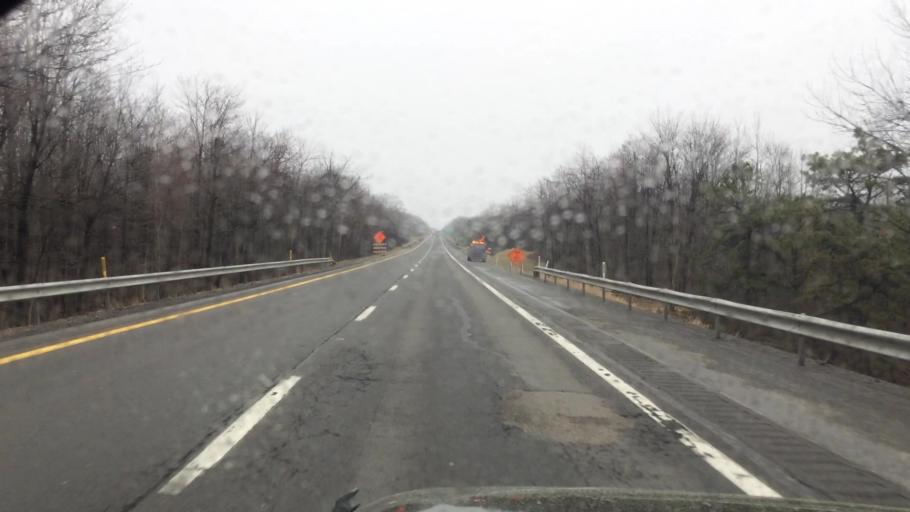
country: US
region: Pennsylvania
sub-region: Schuylkill County
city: Girardville
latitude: 40.7600
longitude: -76.2765
